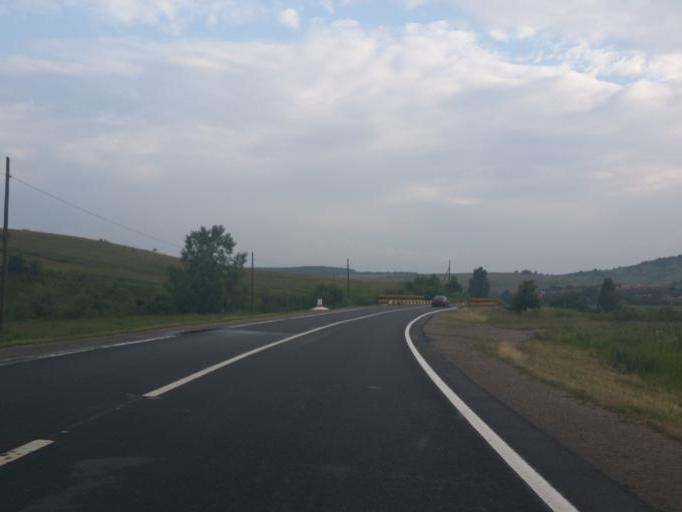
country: RO
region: Cluj
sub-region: Comuna Sanpaul
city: Sanpaul
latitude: 46.8613
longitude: 23.4086
